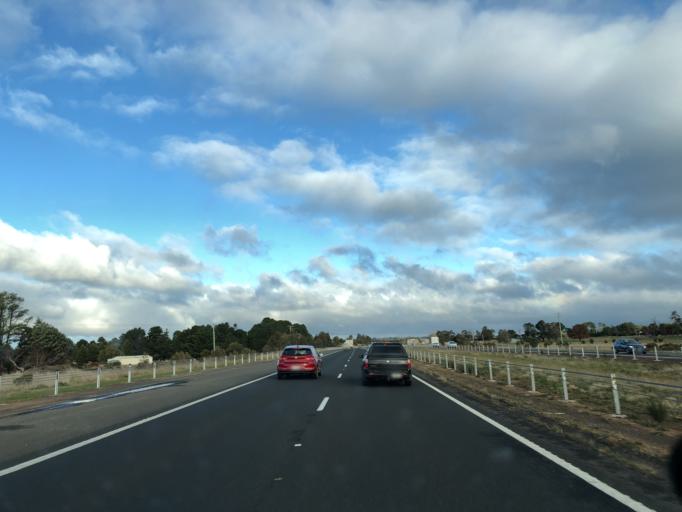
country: AU
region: Victoria
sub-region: Mount Alexander
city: Castlemaine
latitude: -37.2053
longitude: 144.4093
